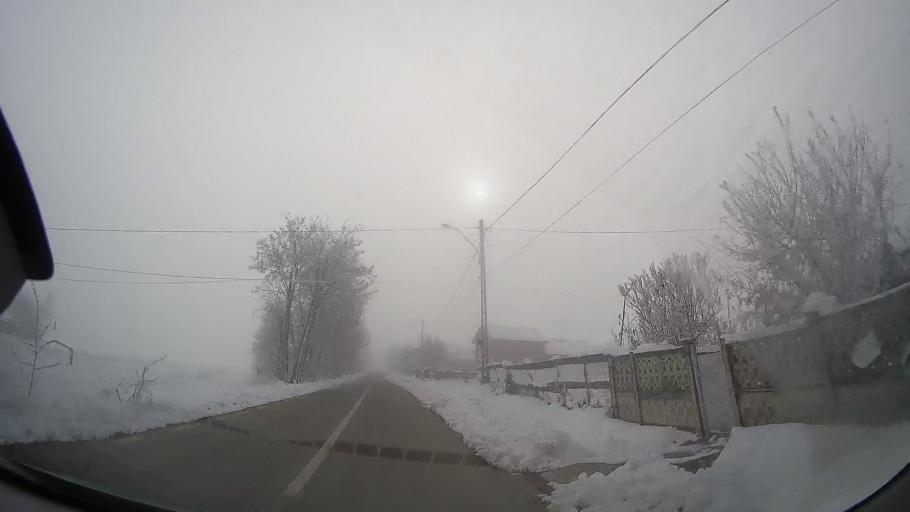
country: RO
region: Iasi
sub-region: Comuna Valea Seaca
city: Valea Seaca
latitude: 47.2839
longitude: 26.6692
